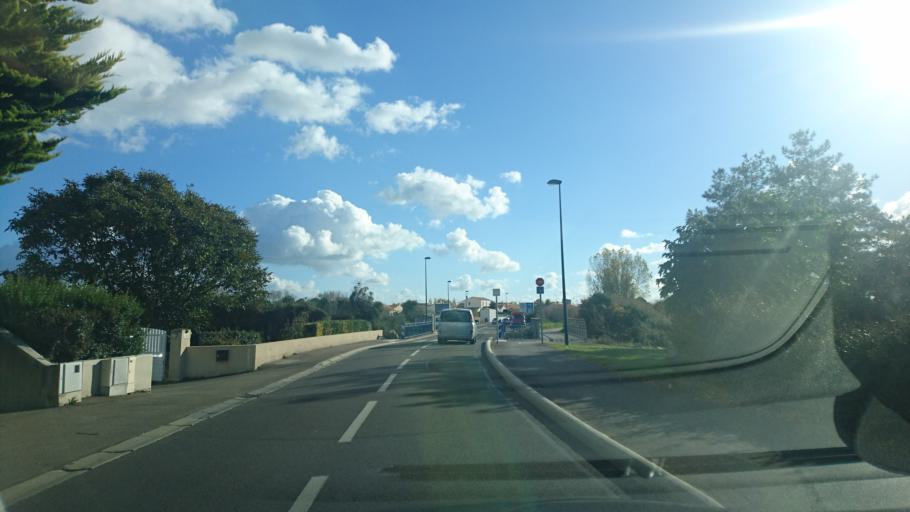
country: FR
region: Pays de la Loire
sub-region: Departement de la Vendee
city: Les Sables-d'Olonne
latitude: 46.5180
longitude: -1.7912
